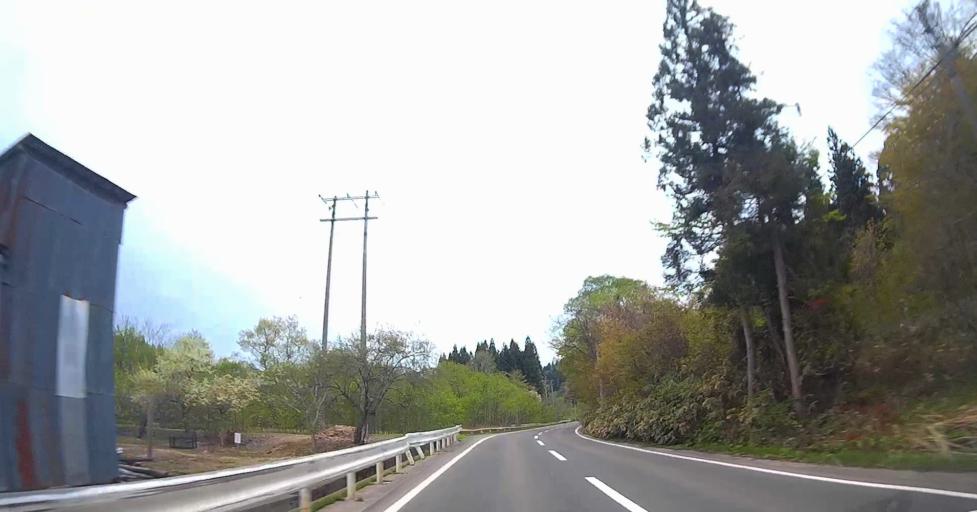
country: JP
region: Aomori
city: Goshogawara
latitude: 41.1286
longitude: 140.5198
